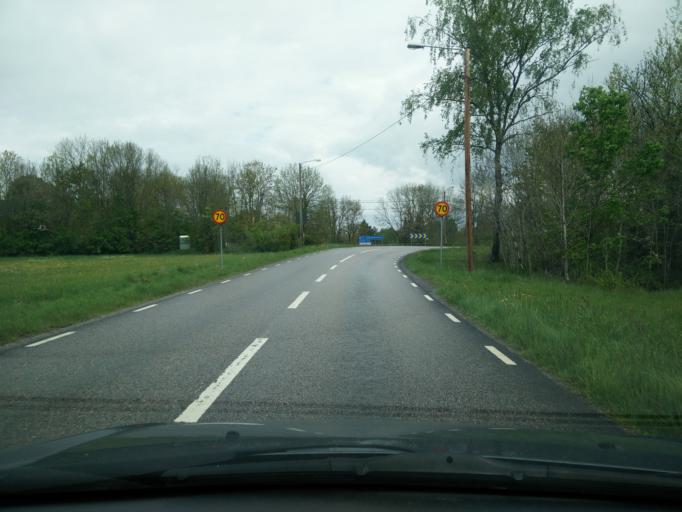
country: SE
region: Stockholm
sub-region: Norrtalje Kommun
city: Bjorko
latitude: 59.8156
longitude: 18.8927
